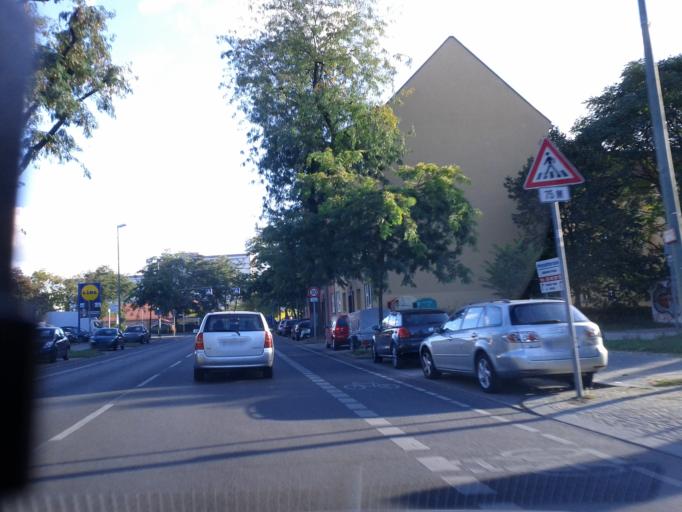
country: DE
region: Berlin
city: Fennpfuhl
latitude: 52.5216
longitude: 13.4859
